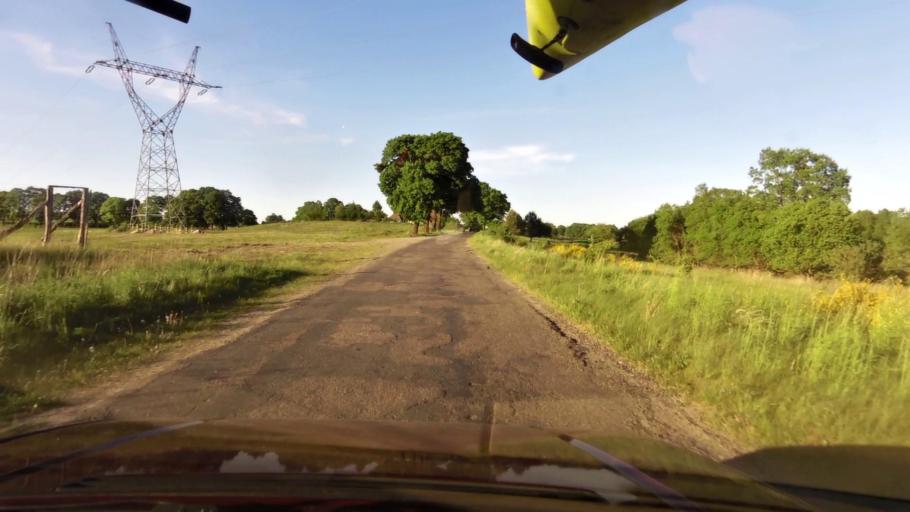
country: PL
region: West Pomeranian Voivodeship
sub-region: Powiat szczecinecki
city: Bialy Bor
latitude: 53.9463
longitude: 16.7713
